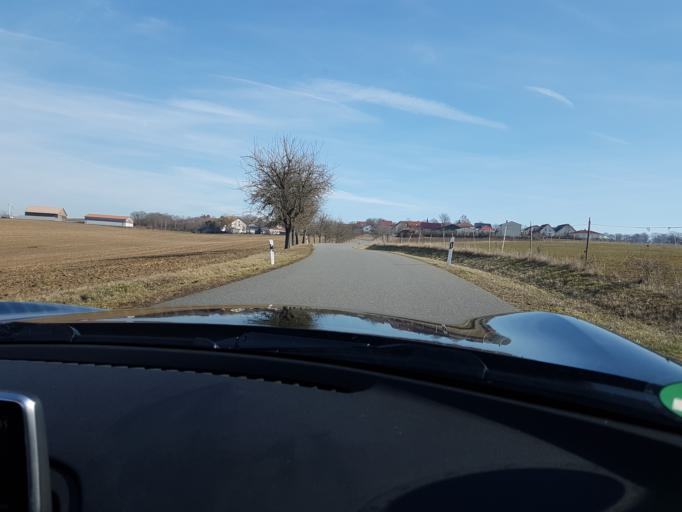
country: DE
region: Baden-Wuerttemberg
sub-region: Karlsruhe Region
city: Rosenberg
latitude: 49.4434
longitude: 9.4766
